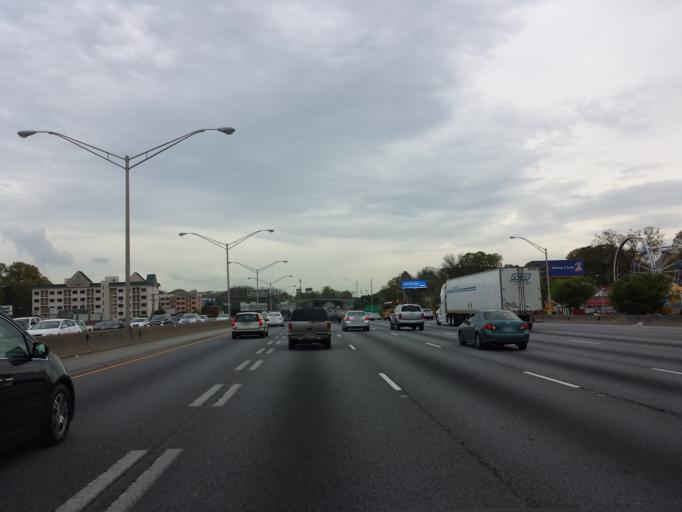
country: US
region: Georgia
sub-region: Fulton County
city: Atlanta
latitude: 33.7364
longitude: -84.3921
